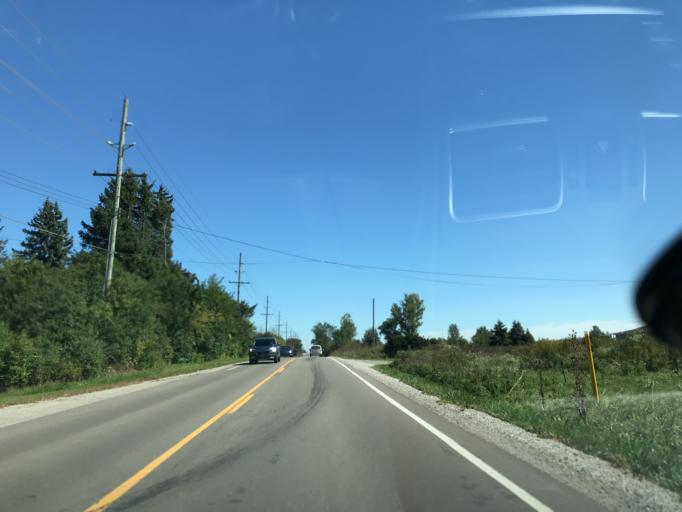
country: US
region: Michigan
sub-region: Washtenaw County
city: Ypsilanti
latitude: 42.2751
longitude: -83.6165
